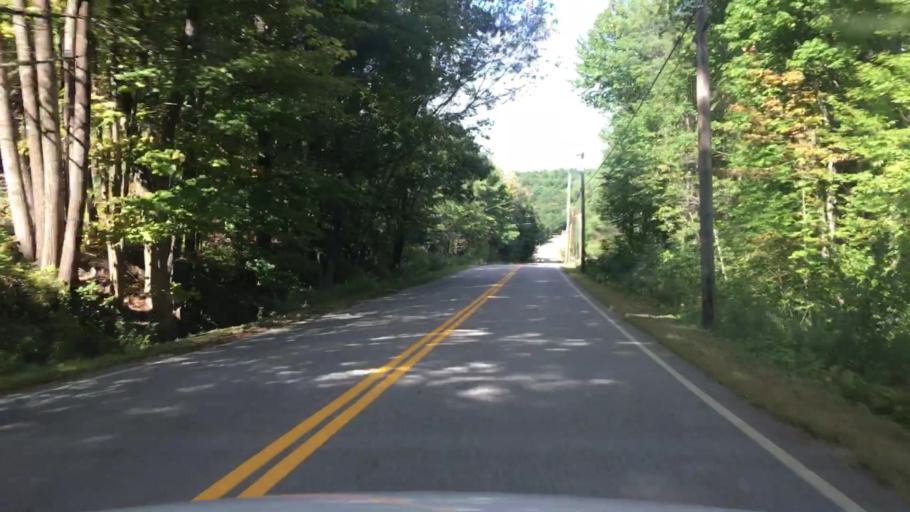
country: US
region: Maine
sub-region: Cumberland County
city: West Scarborough
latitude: 43.6242
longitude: -70.4081
